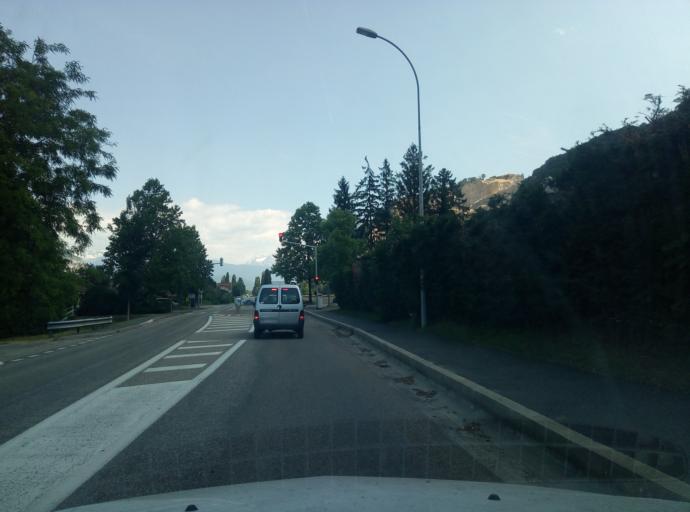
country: FR
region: Rhone-Alpes
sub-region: Departement de l'Isere
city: Noyarey
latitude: 45.2370
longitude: 5.6371
